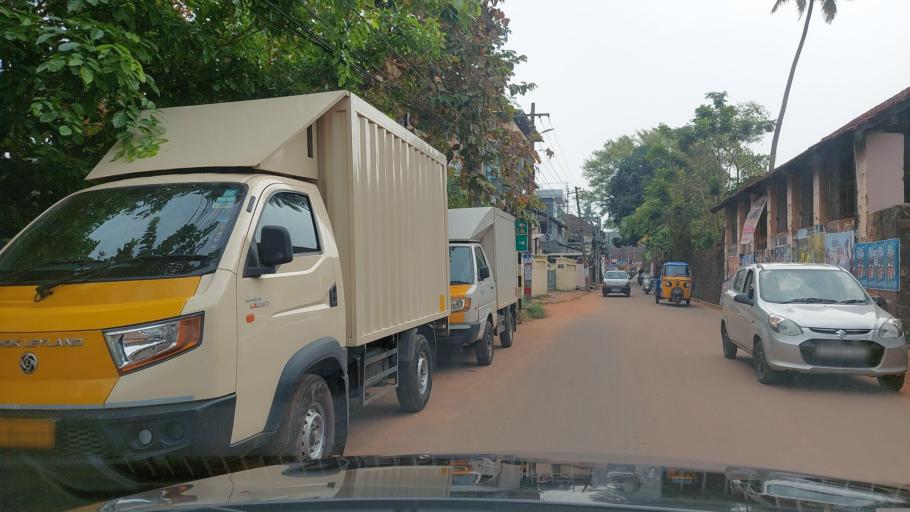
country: IN
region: Kerala
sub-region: Kozhikode
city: Kozhikode
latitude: 11.2489
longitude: 75.7888
